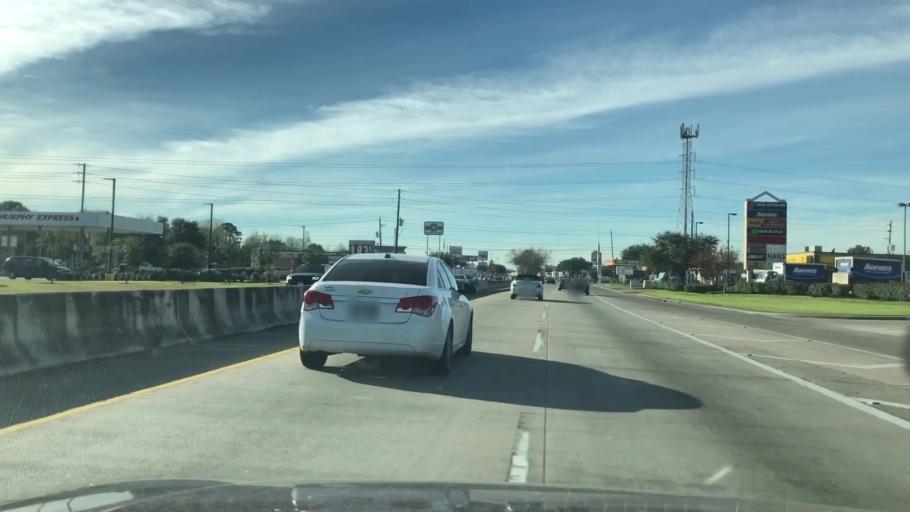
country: US
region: Texas
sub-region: Harris County
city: Bellaire
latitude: 29.6688
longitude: -95.4626
